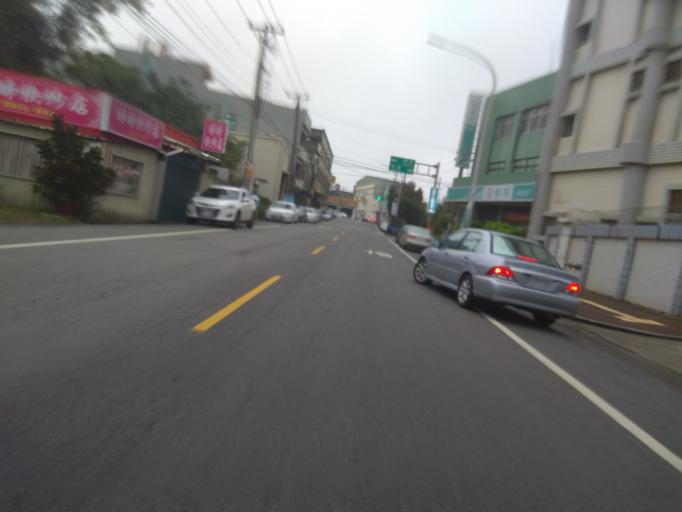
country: TW
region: Taiwan
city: Taoyuan City
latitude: 25.0111
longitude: 121.1370
